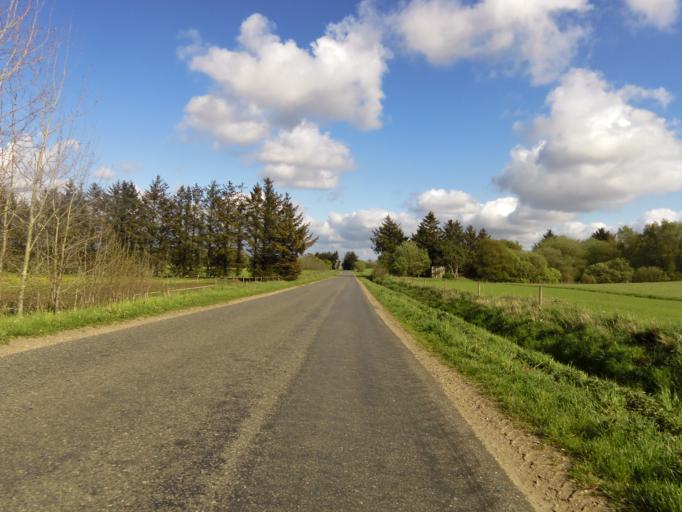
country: DK
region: South Denmark
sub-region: Esbjerg Kommune
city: Ribe
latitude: 55.2630
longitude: 8.7580
